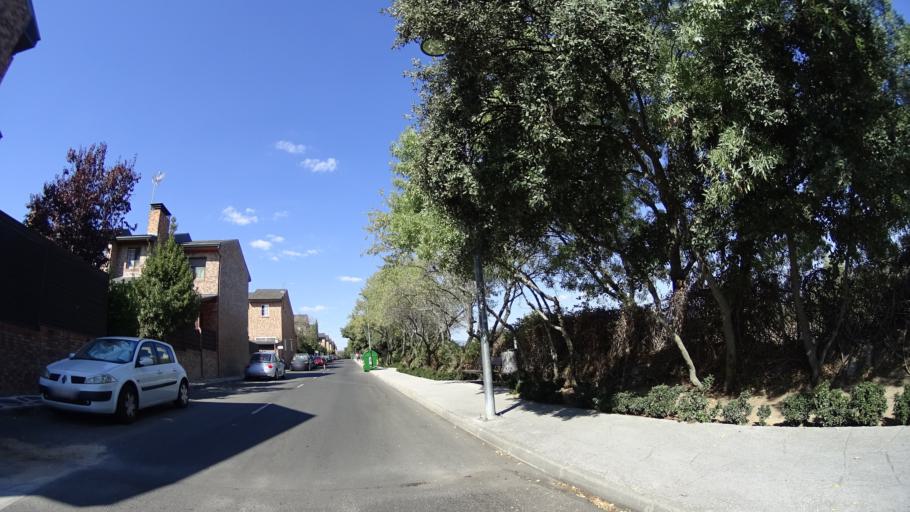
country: ES
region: Madrid
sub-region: Provincia de Madrid
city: Navalquejigo
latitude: 40.6085
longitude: -4.0265
